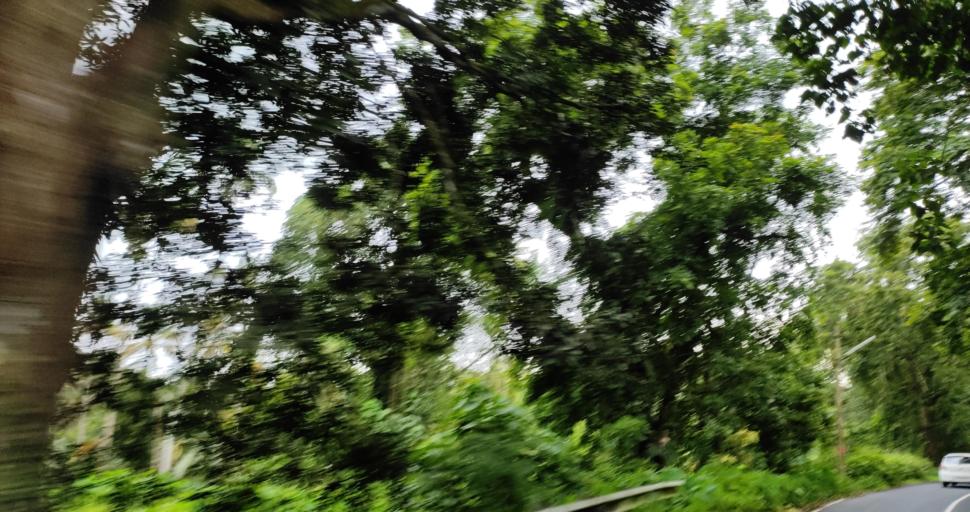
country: IN
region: Kerala
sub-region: Thrissur District
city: Kizhake Chalakudi
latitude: 10.3020
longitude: 76.4484
